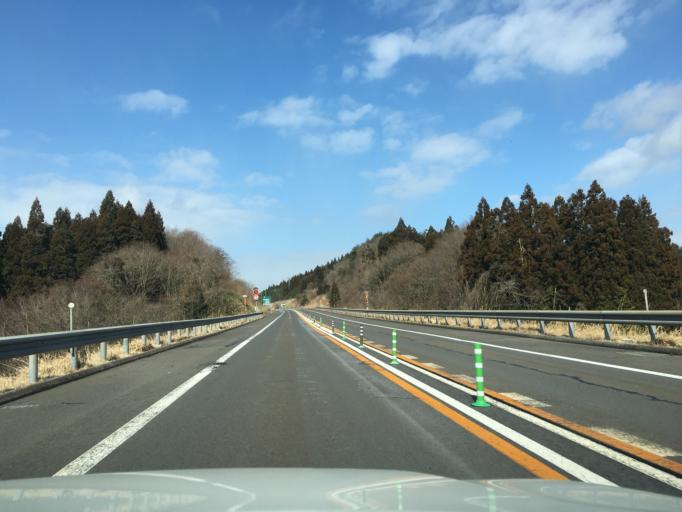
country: JP
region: Akita
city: Akita
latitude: 39.7455
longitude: 140.1585
